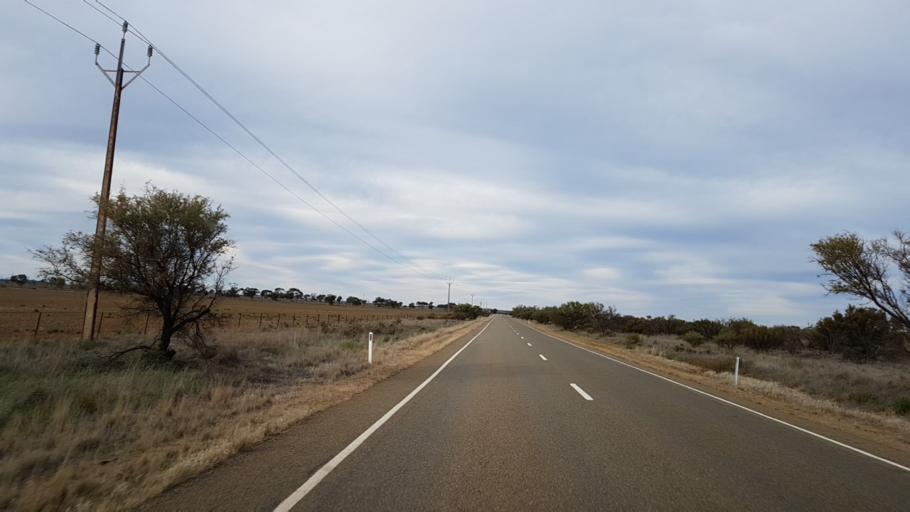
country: AU
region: South Australia
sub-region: Peterborough
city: Peterborough
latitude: -32.9957
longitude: 138.7841
